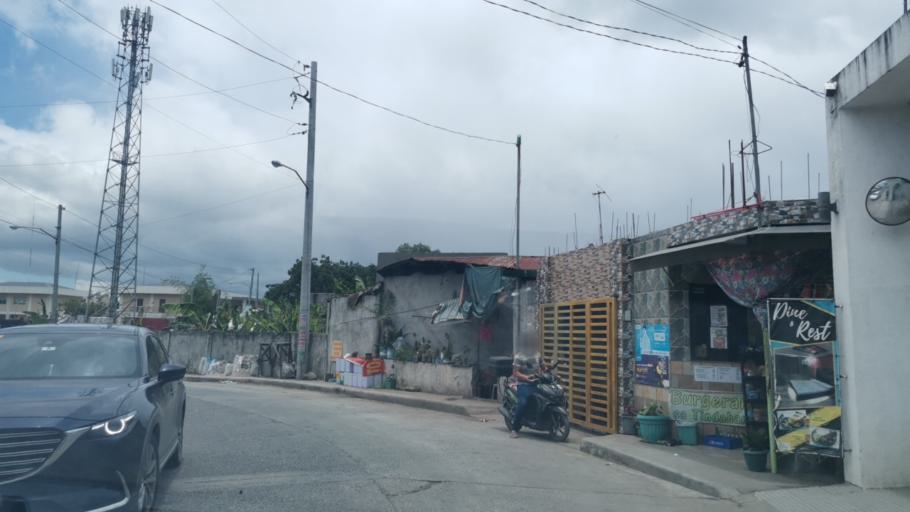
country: PH
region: Calabarzon
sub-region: Province of Batangas
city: Tanauan
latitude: 14.0859
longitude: 121.1378
